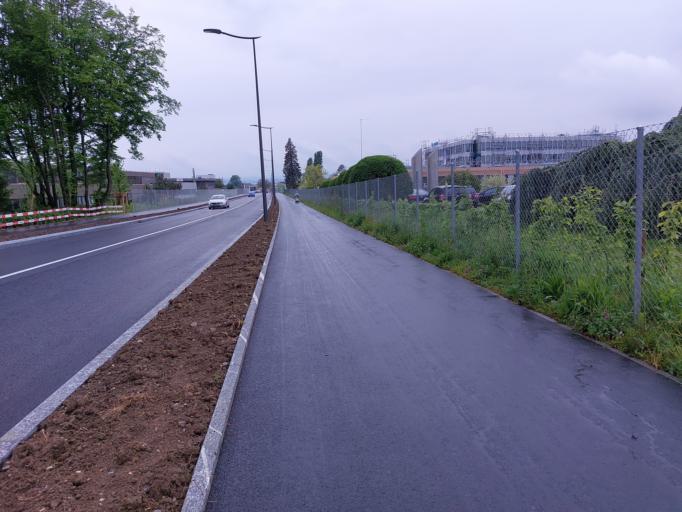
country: CH
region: Vaud
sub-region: Ouest Lausannois District
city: Ecublens
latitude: 46.5139
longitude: 6.5540
